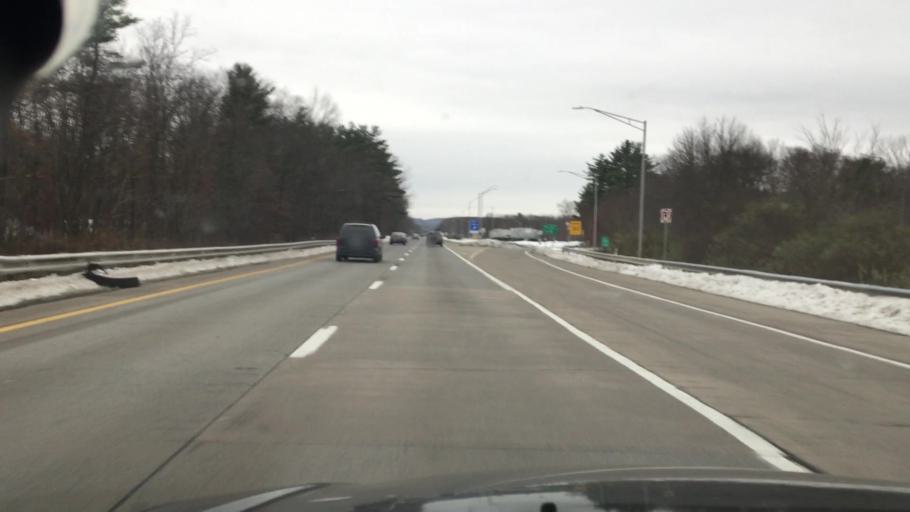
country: US
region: Pennsylvania
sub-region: Luzerne County
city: Nanticoke
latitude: 41.1335
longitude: -75.9632
